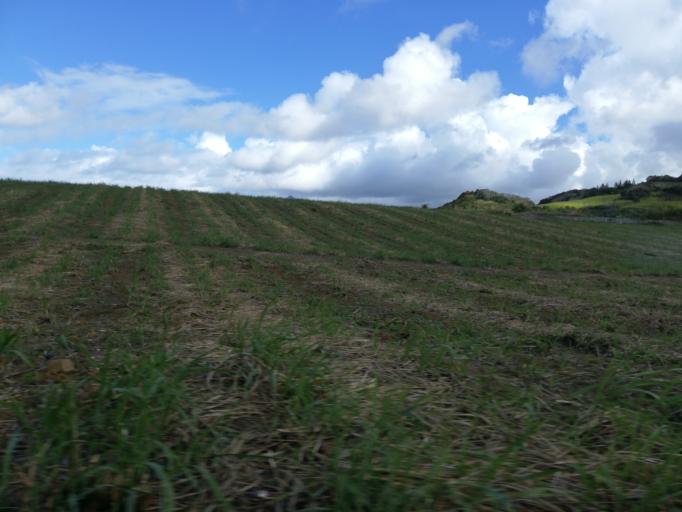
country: MU
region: Flacq
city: Bel Air Riviere Seche
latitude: -20.2638
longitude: 57.7384
